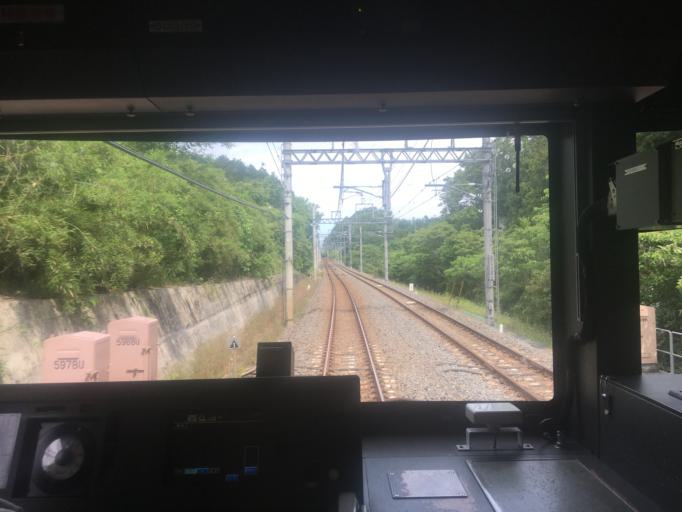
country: JP
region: Saitama
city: Ogawa
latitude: 36.0532
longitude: 139.3035
